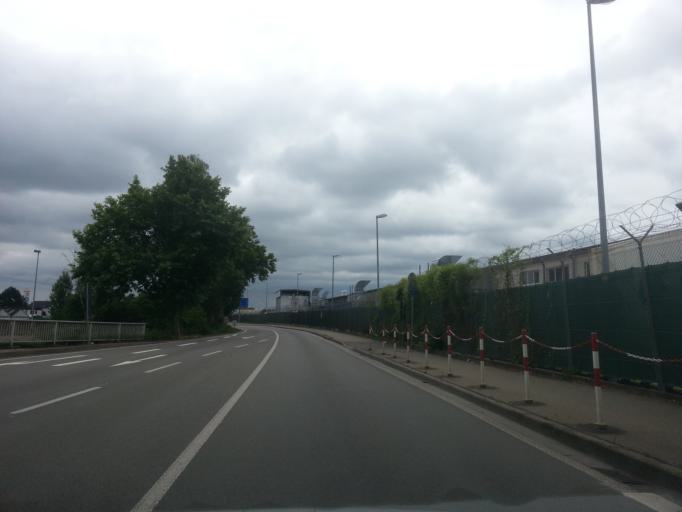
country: DE
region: Rheinland-Pfalz
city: Grunstadt
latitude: 49.5552
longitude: 8.1773
